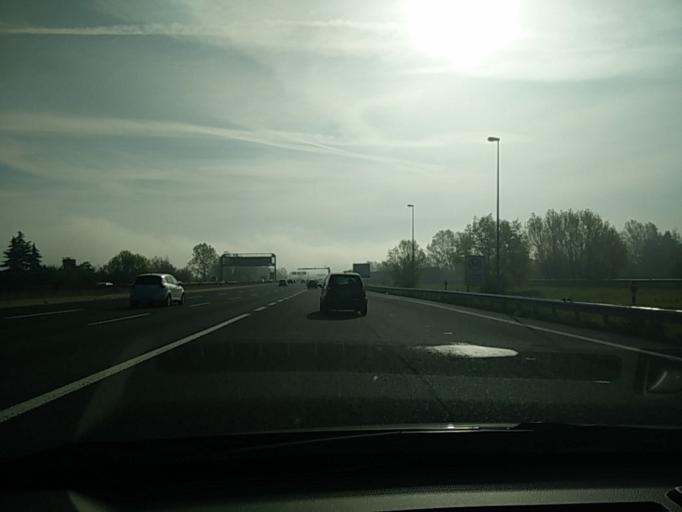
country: IT
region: Emilia-Romagna
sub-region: Provincia di Bologna
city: Villanova
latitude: 44.4805
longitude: 11.4330
